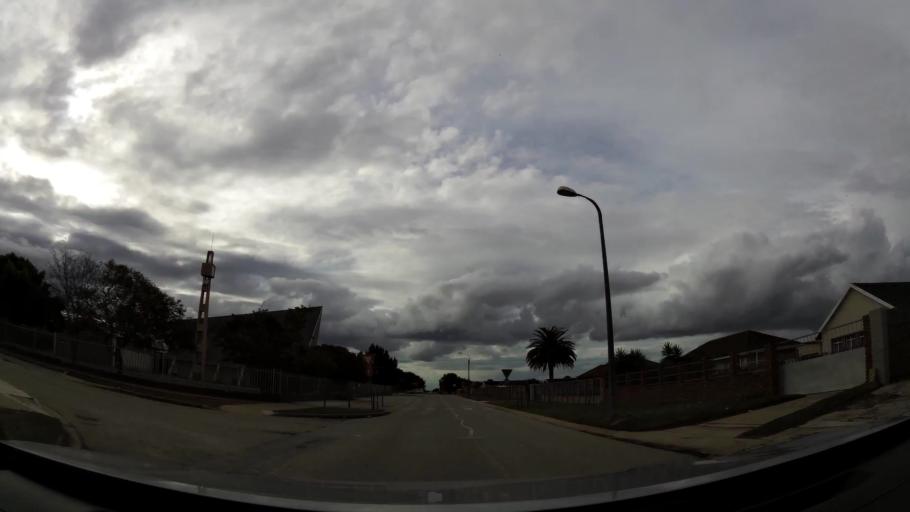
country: ZA
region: Eastern Cape
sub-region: Nelson Mandela Bay Metropolitan Municipality
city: Port Elizabeth
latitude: -33.9436
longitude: 25.4946
